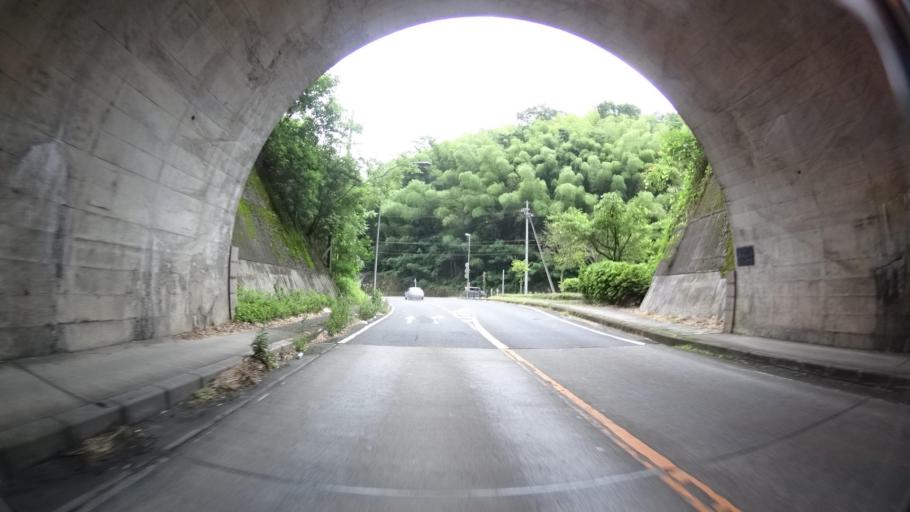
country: JP
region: Kyoto
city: Maizuru
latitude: 35.4666
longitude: 135.3753
